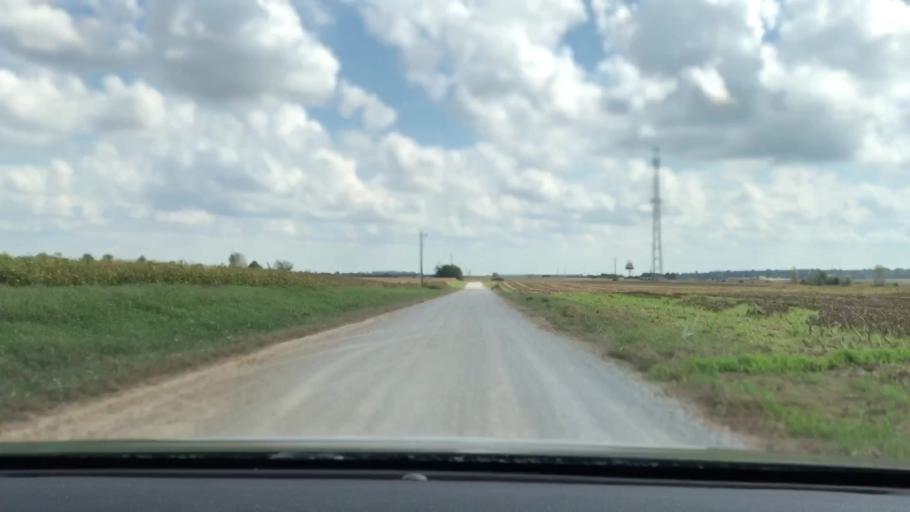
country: US
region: Kentucky
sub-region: Christian County
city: Oak Grove
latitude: 36.6841
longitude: -87.4153
